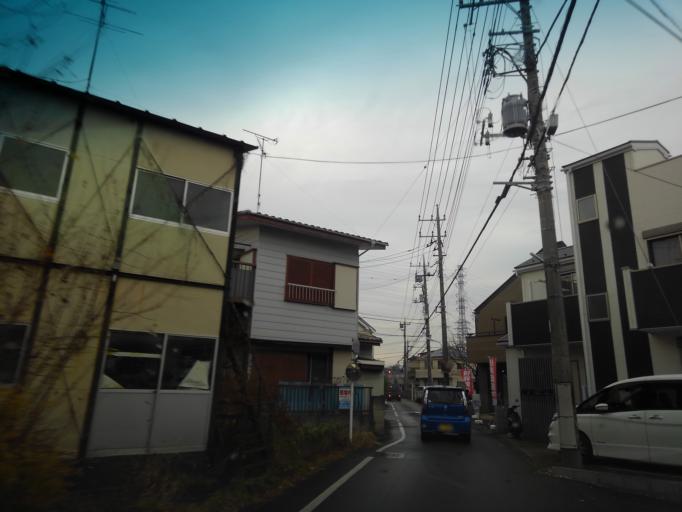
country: JP
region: Tokyo
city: Kokubunji
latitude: 35.7130
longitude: 139.4447
